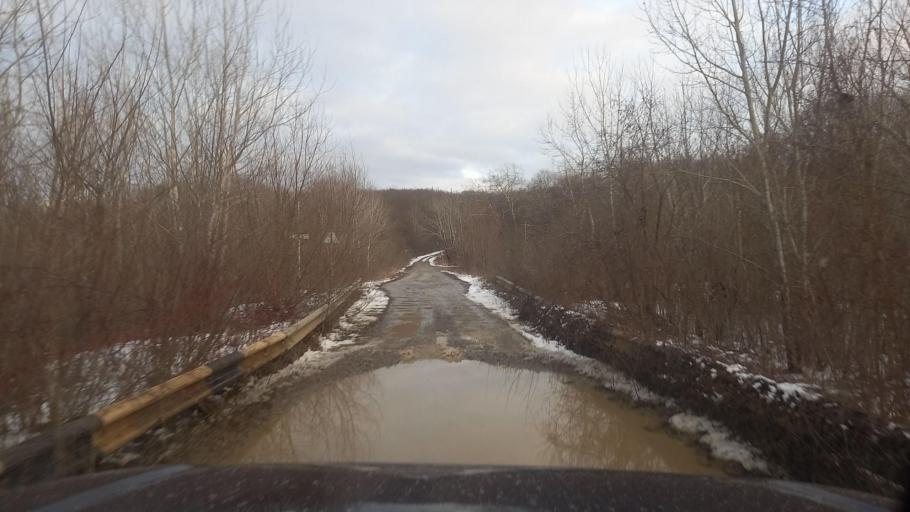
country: RU
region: Krasnodarskiy
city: Smolenskaya
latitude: 44.6791
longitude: 38.7819
